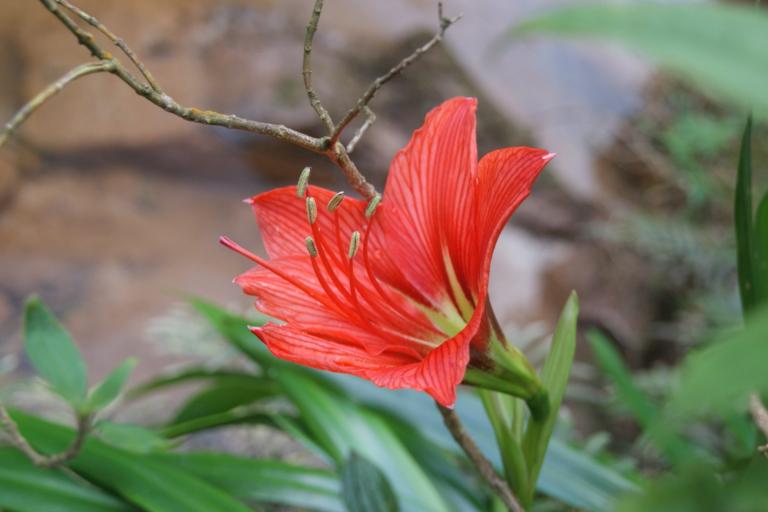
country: BR
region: Sao Paulo
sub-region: Cubatao
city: Cubatao
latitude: -23.8312
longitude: -46.4383
